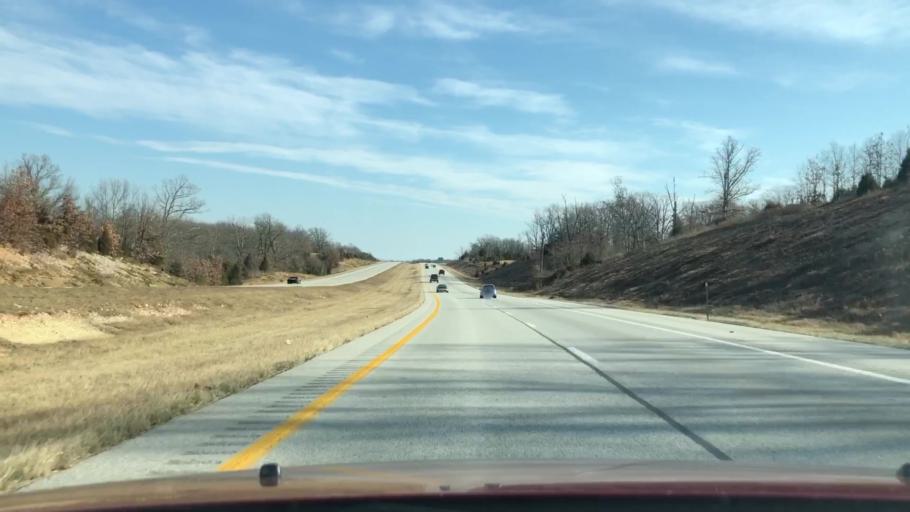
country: US
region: Missouri
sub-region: Webster County
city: Seymour
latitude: 37.1610
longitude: -92.8933
